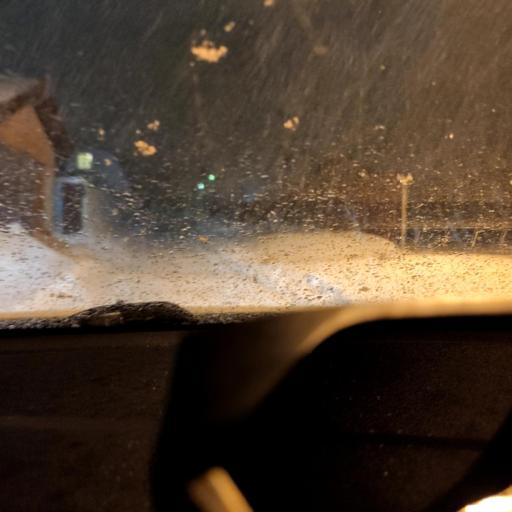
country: RU
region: Tatarstan
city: Stolbishchi
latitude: 55.7480
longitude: 49.2957
